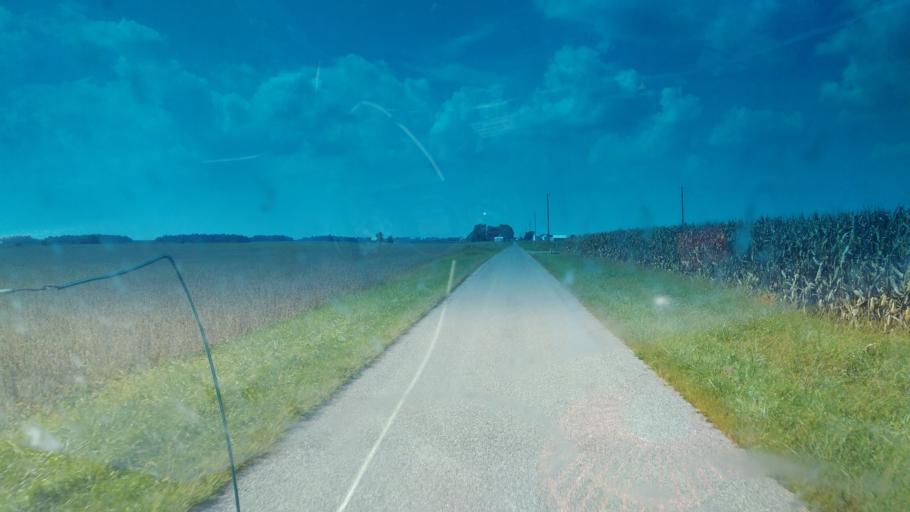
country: US
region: Ohio
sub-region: Hardin County
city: Ada
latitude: 40.6819
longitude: -83.8674
